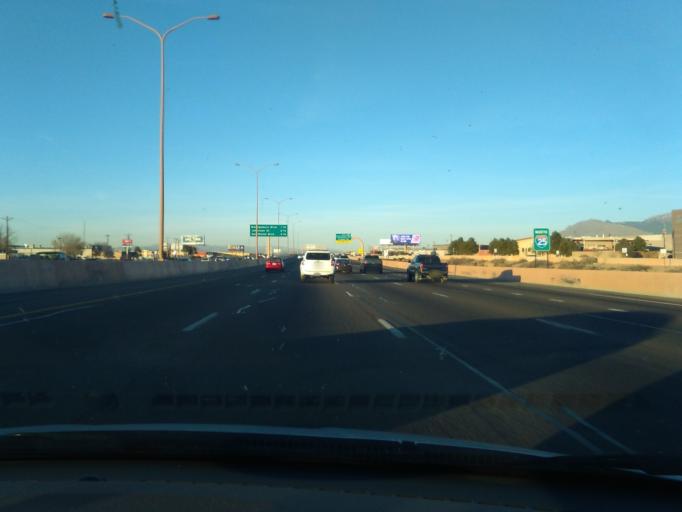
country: US
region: New Mexico
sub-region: Bernalillo County
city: Lee Acres
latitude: 35.1172
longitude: -106.6247
